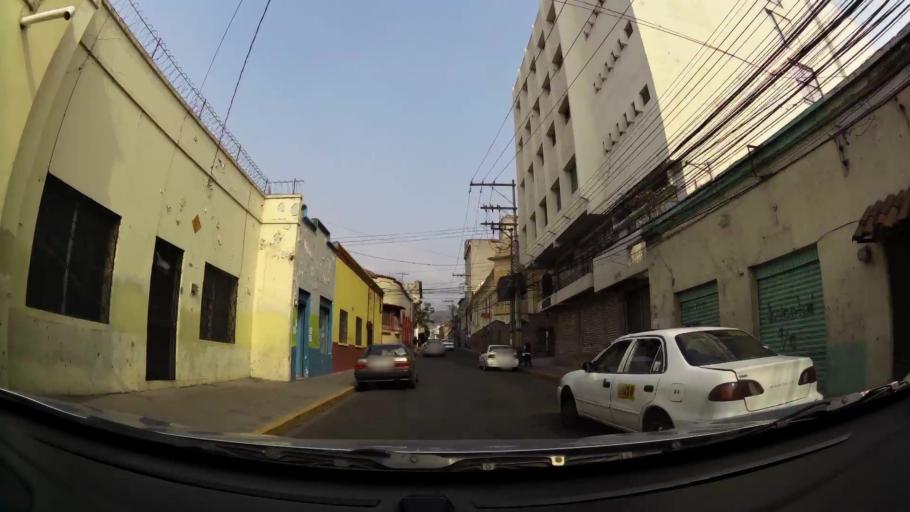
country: HN
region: Francisco Morazan
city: Tegucigalpa
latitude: 14.1049
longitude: -87.2006
